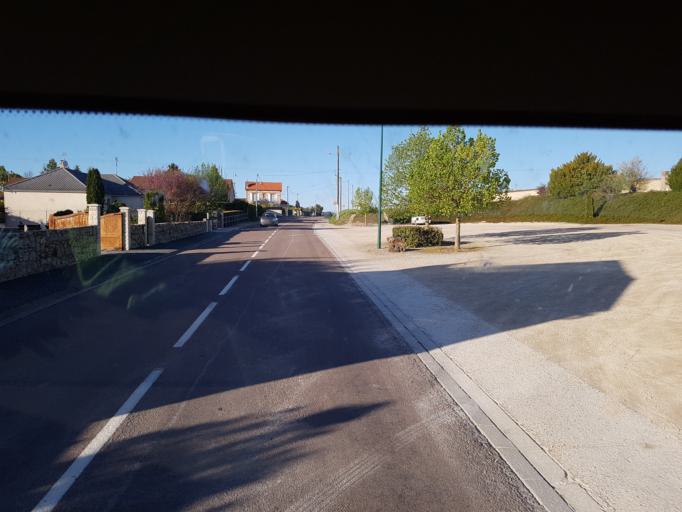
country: FR
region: Champagne-Ardenne
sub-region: Departement de l'Aube
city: Marigny-le-Chatel
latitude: 48.4409
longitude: 3.6819
